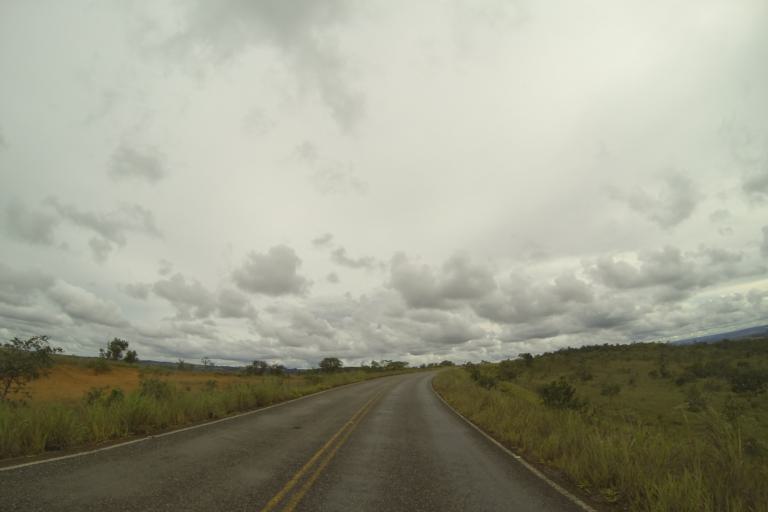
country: BR
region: Minas Gerais
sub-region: Ibia
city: Ibia
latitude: -19.6780
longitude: -46.4415
